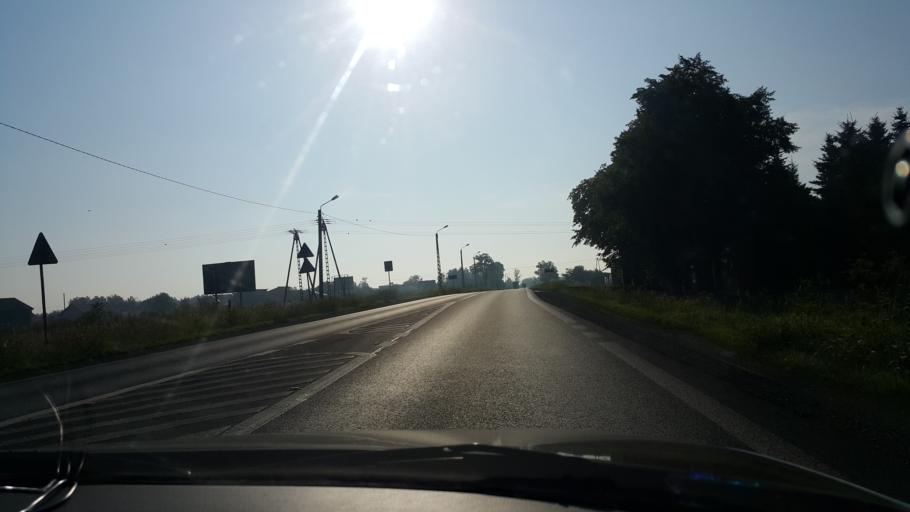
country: PL
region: Masovian Voivodeship
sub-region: Radom
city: Radom
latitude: 51.4139
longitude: 21.2225
